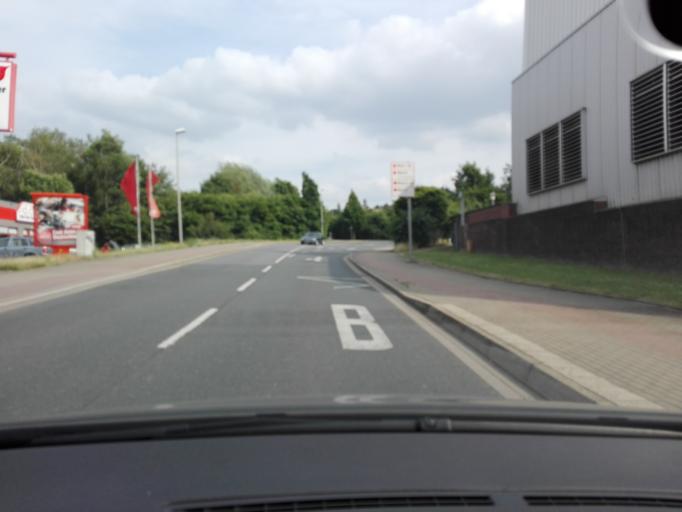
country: DE
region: North Rhine-Westphalia
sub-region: Regierungsbezirk Arnsberg
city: Unna
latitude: 51.5393
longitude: 7.6723
